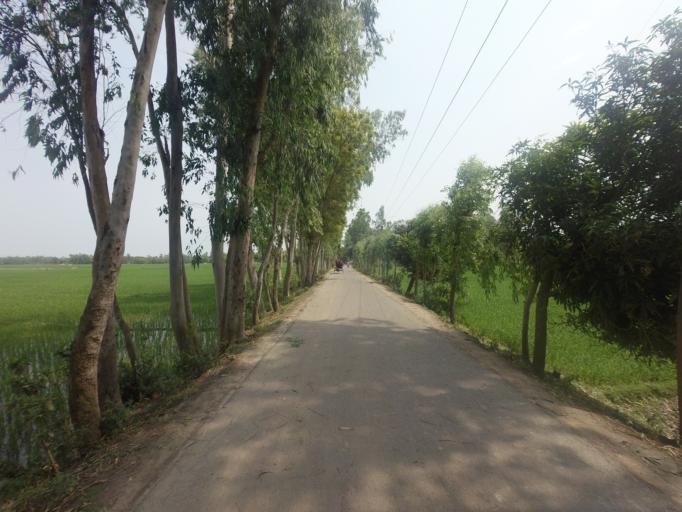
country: BD
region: Rajshahi
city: Sirajganj
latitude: 24.3601
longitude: 89.7078
